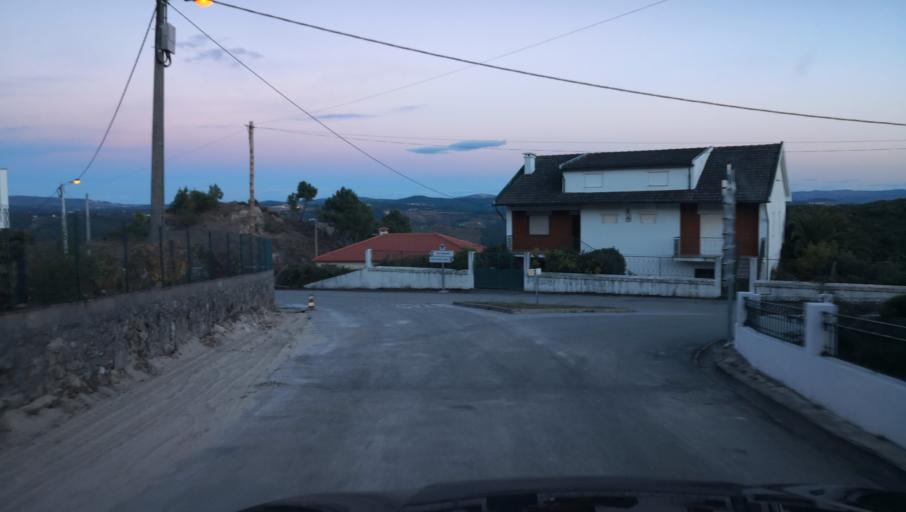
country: PT
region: Vila Real
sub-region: Santa Marta de Penaguiao
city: Santa Marta de Penaguiao
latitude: 41.2597
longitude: -7.7817
